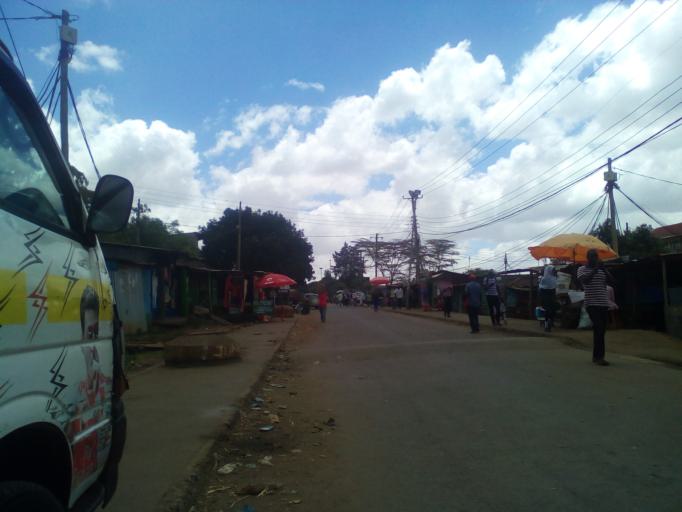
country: KE
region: Nairobi Area
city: Nairobi
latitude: -1.3104
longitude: 36.7811
